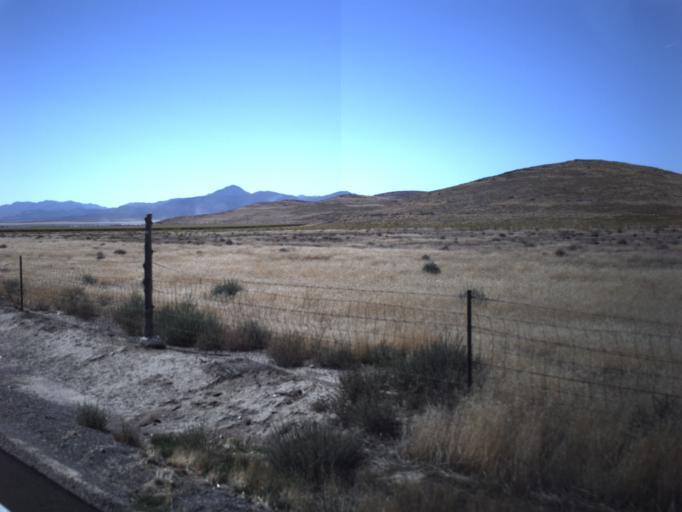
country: US
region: Utah
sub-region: Utah County
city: Eagle Mountain
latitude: 40.1456
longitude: -111.9496
